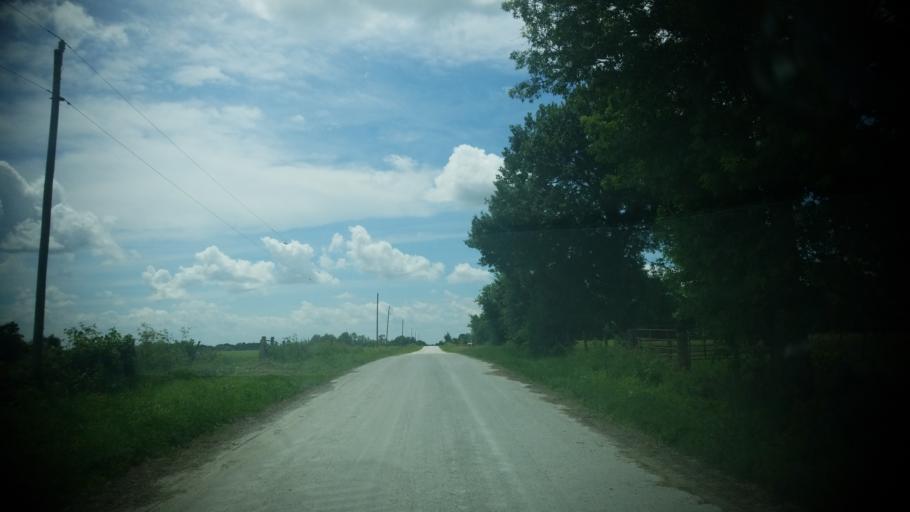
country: US
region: Missouri
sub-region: Pike County
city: Bowling Green
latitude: 39.3084
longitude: -91.3074
